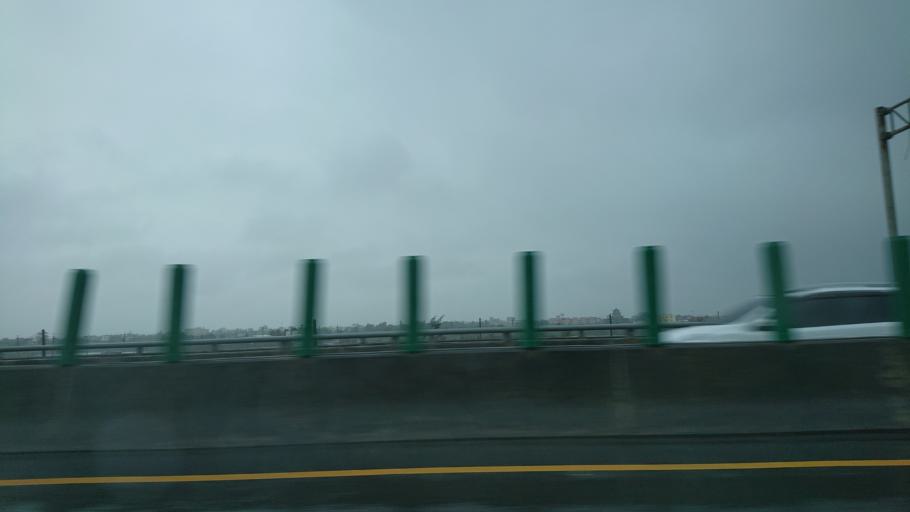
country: TW
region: Taiwan
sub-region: Chiayi
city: Taibao
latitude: 23.7121
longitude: 120.1923
